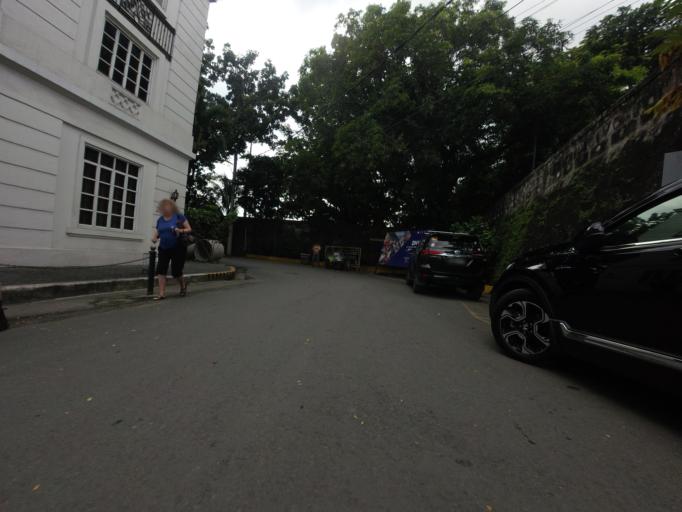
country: PH
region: Metro Manila
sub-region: City of Manila
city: Port Area
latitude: 14.5924
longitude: 120.9716
